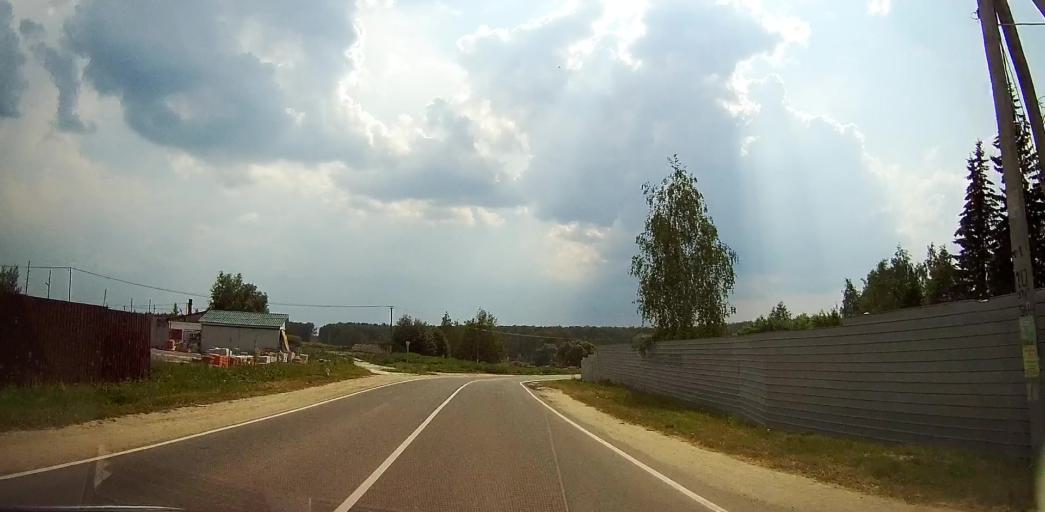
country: RU
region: Moskovskaya
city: Zhilevo
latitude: 55.0526
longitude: 37.9897
